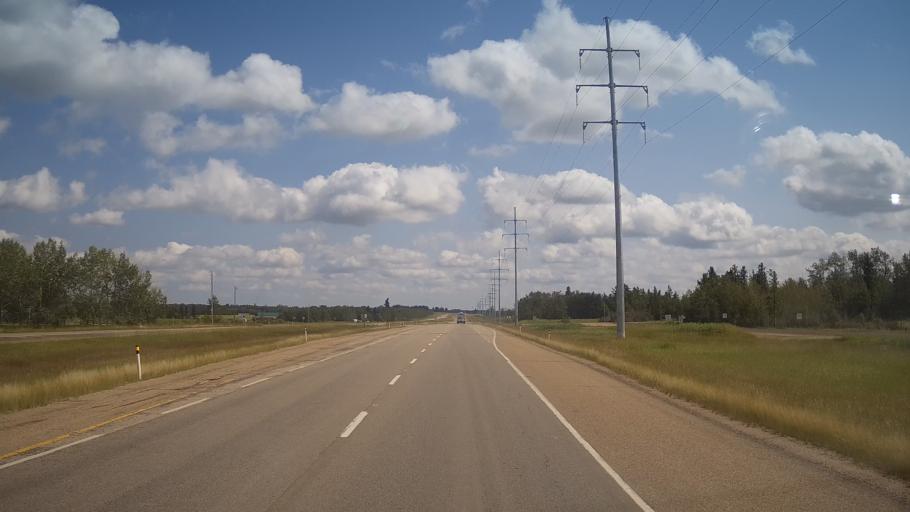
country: CA
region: Alberta
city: Sherwood Park
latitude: 53.4426
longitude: -113.2244
